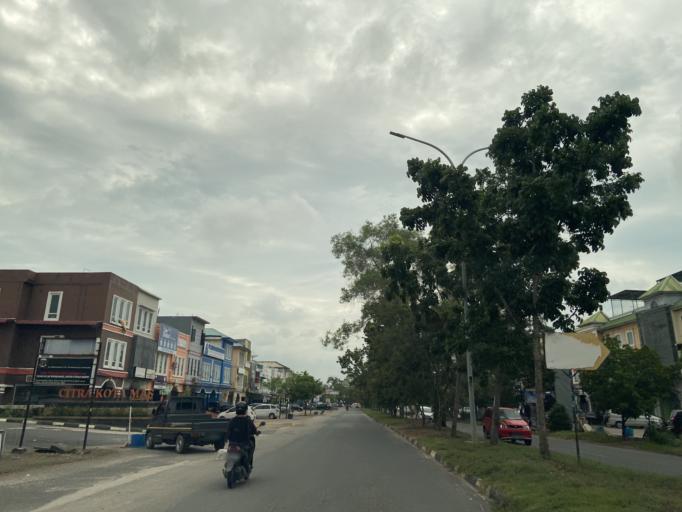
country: SG
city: Singapore
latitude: 1.1239
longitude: 104.0478
